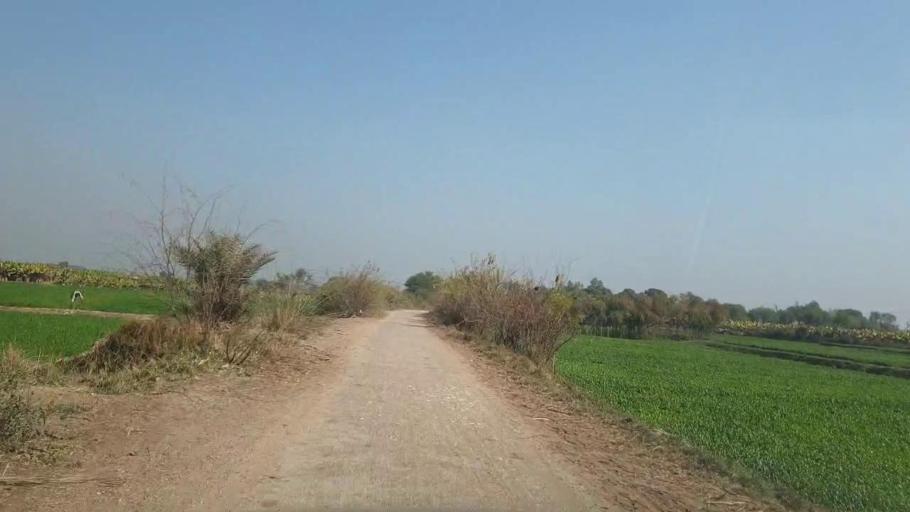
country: PK
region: Sindh
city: Matiari
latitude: 25.5476
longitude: 68.4894
